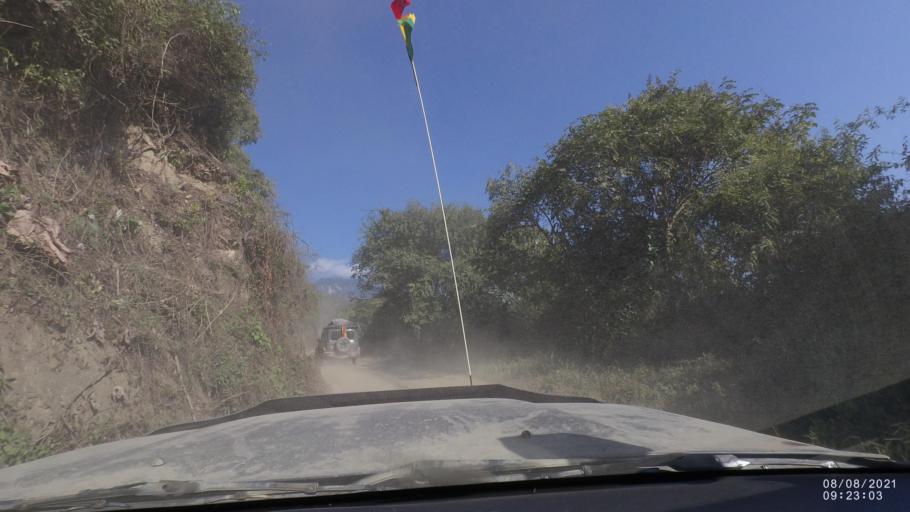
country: BO
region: La Paz
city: Quime
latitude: -16.5774
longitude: -66.7175
